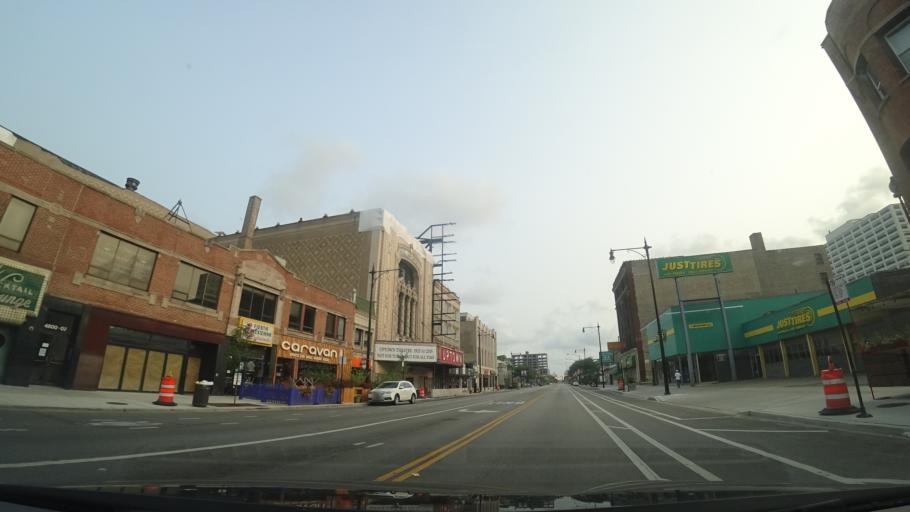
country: US
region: Illinois
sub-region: Cook County
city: Evanston
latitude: 41.9692
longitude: -87.6596
